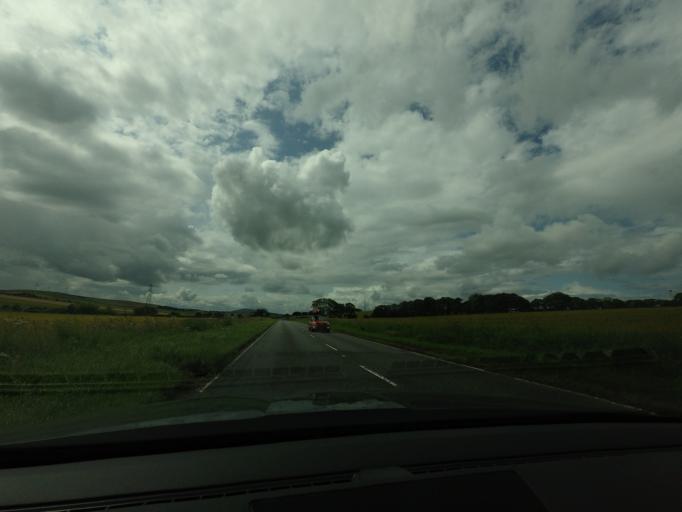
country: GB
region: Scotland
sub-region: Aberdeenshire
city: Whitehills
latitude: 57.6589
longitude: -2.5989
